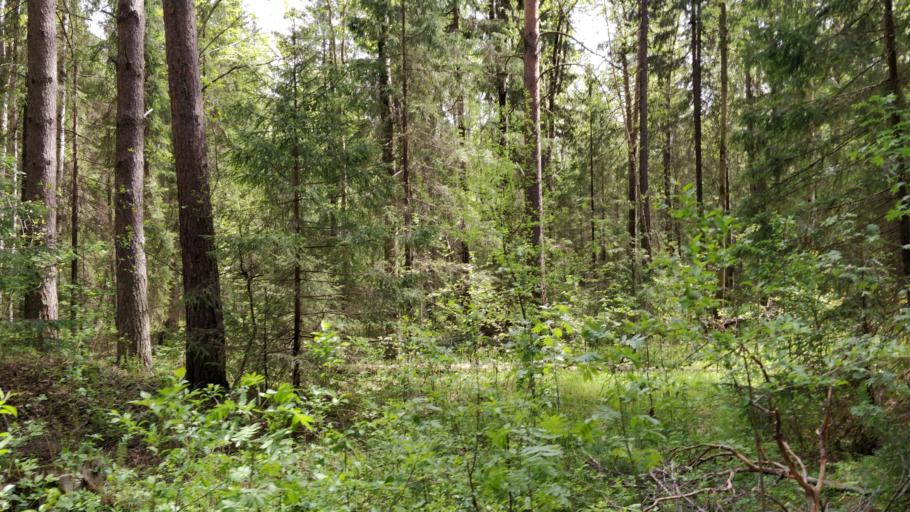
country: RU
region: Perm
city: Kondratovo
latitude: 57.9816
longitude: 56.1478
